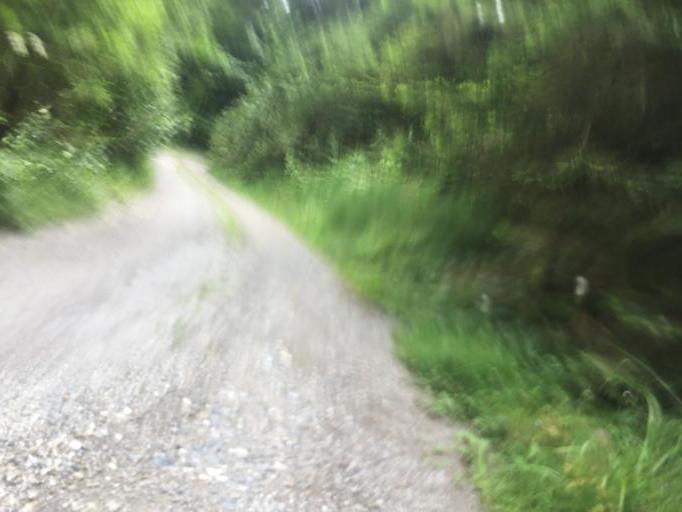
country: CH
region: Bern
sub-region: Thun District
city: Wattenwil
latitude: 46.7510
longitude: 7.4845
